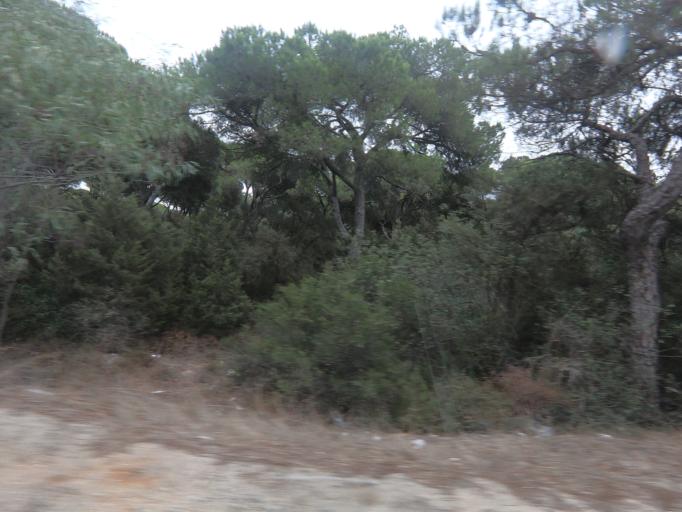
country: PT
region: Setubal
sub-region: Almada
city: Charneca
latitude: 38.5847
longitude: -9.1942
